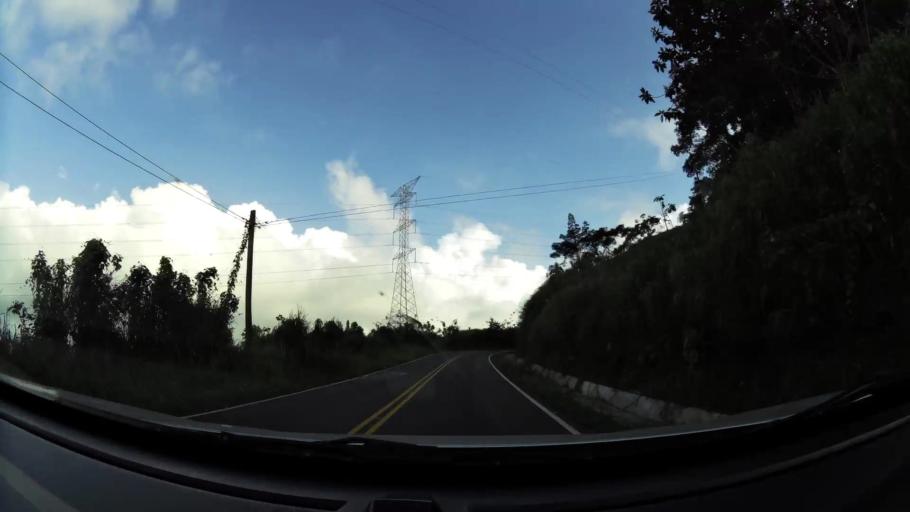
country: CR
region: Limon
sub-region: Canton de Siquirres
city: Siquirres
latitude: 10.0510
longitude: -83.5505
